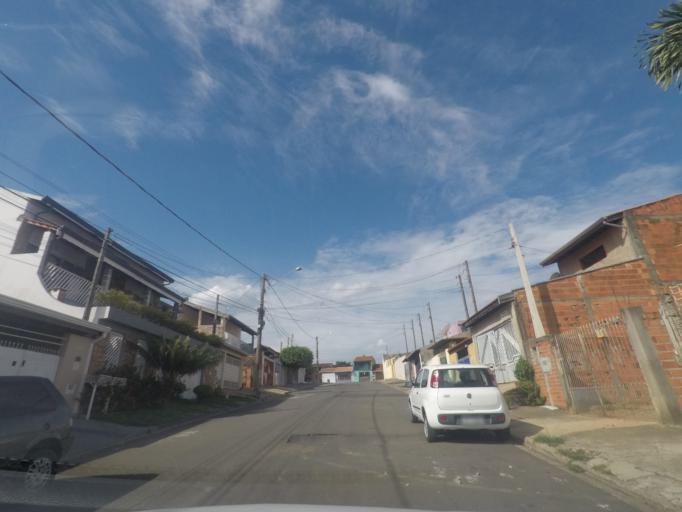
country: BR
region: Sao Paulo
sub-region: Sumare
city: Sumare
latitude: -22.8075
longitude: -47.2662
